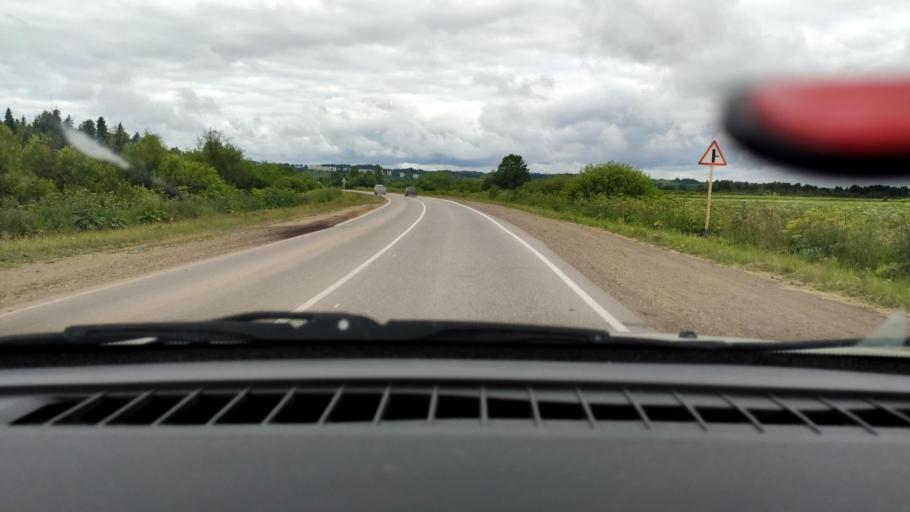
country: RU
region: Perm
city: Chaykovskaya
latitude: 58.0912
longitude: 55.6094
